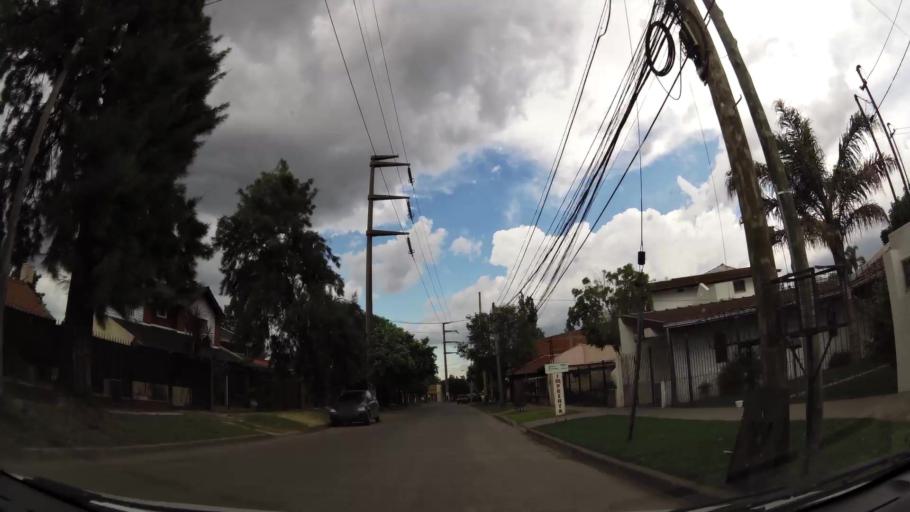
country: AR
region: Buenos Aires
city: Ituzaingo
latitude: -34.6368
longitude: -58.6816
